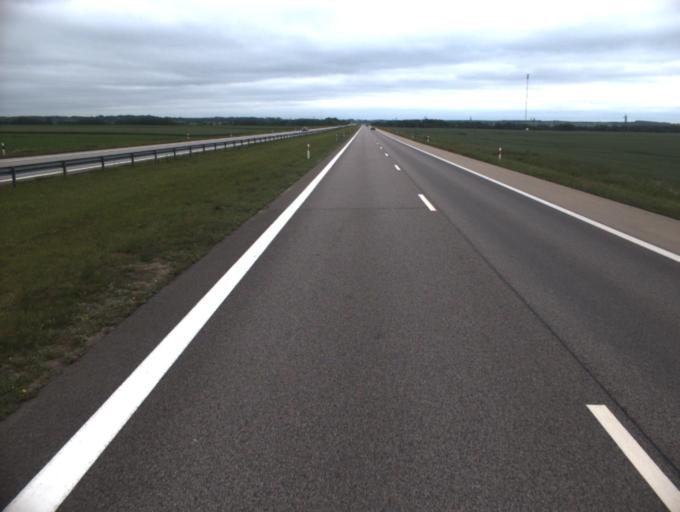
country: LT
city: Raseiniai
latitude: 55.3321
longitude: 23.1231
